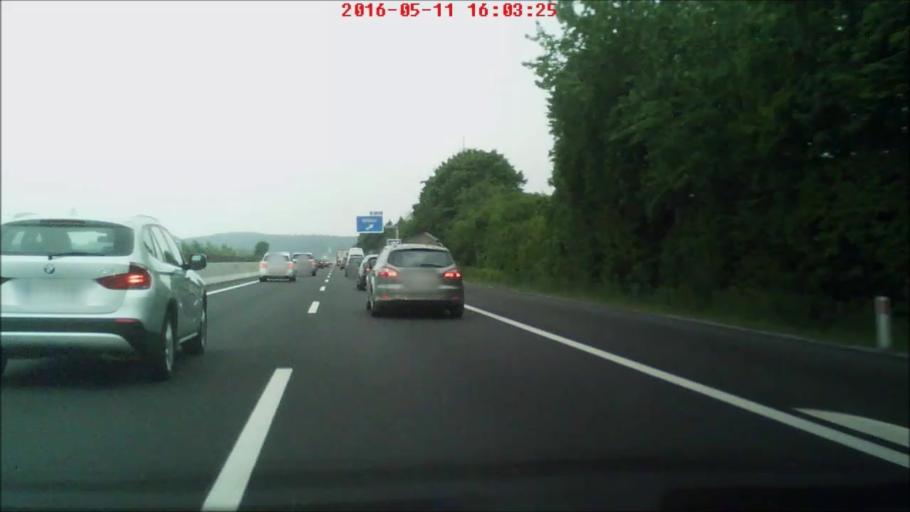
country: AT
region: Styria
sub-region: Politischer Bezirk Leibnitz
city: Weitendorf
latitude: 46.8997
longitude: 15.4721
